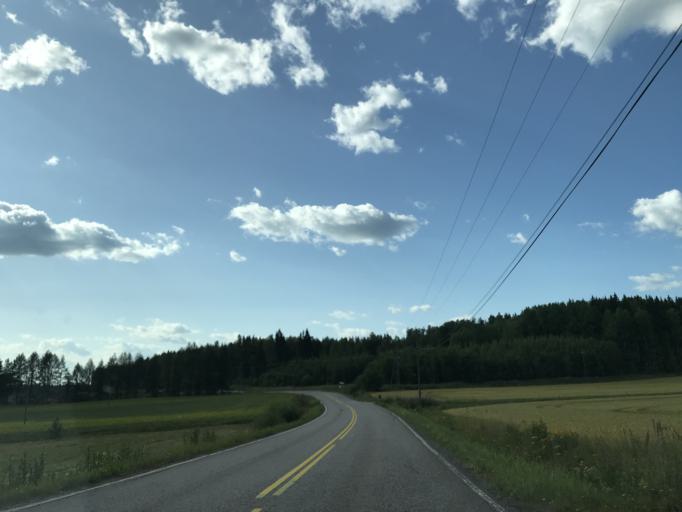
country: FI
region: Uusimaa
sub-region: Helsinki
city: Nurmijaervi
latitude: 60.4504
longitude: 24.6420
